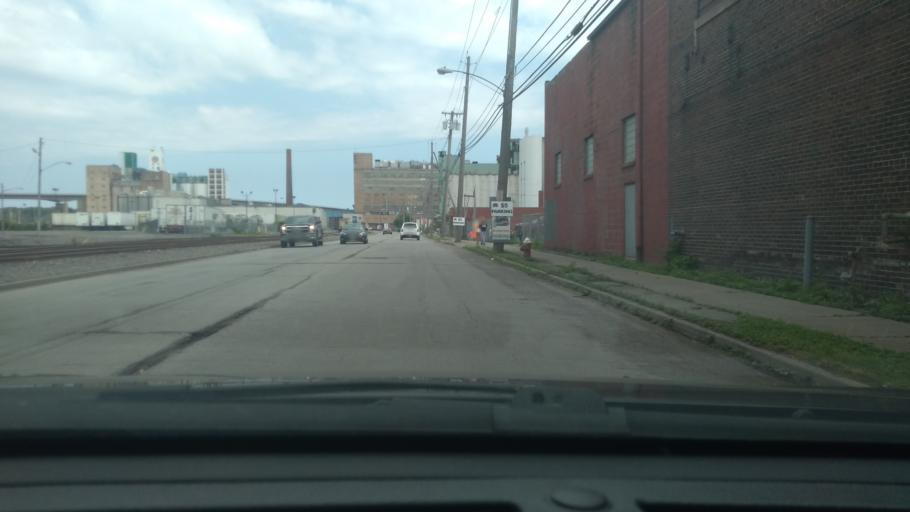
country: US
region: New York
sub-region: Erie County
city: Buffalo
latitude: 42.8675
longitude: -78.8725
